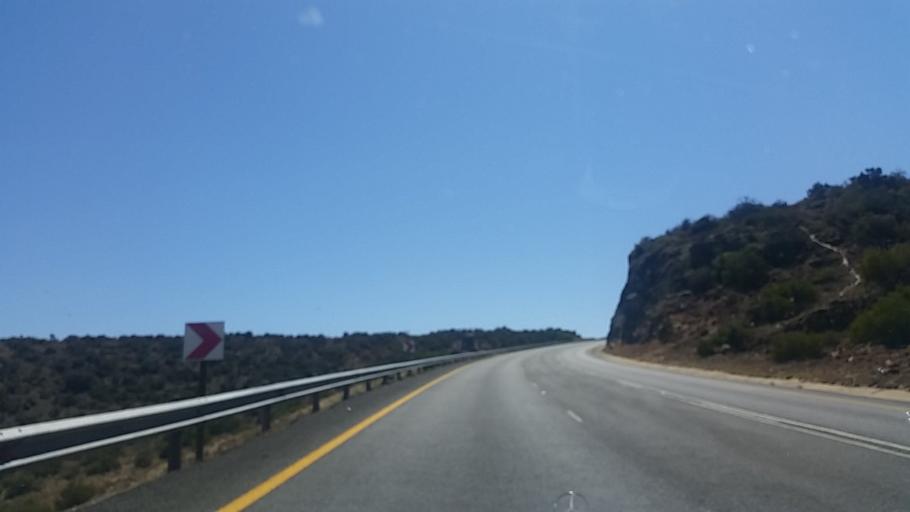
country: ZA
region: Eastern Cape
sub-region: Cacadu District Municipality
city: Graaff-Reinet
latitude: -32.0595
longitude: 24.6084
